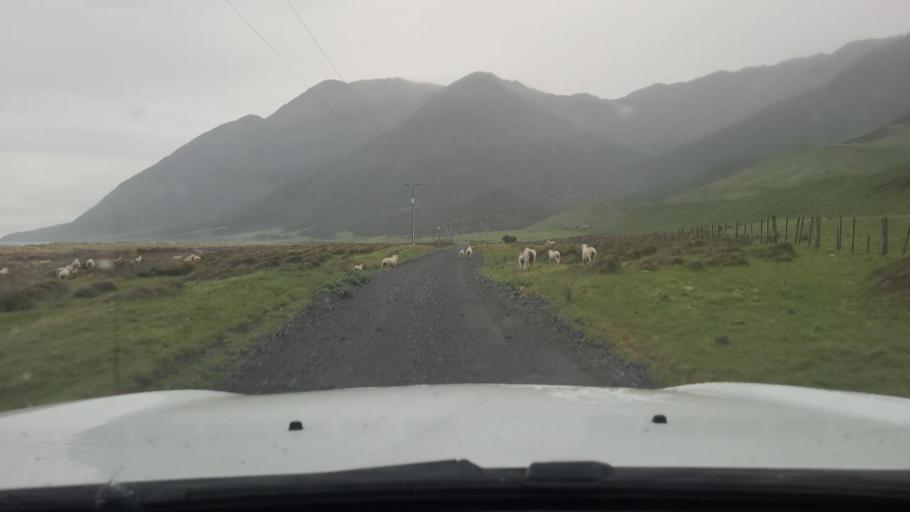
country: NZ
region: Wellington
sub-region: South Wairarapa District
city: Waipawa
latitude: -41.5676
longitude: 175.3807
